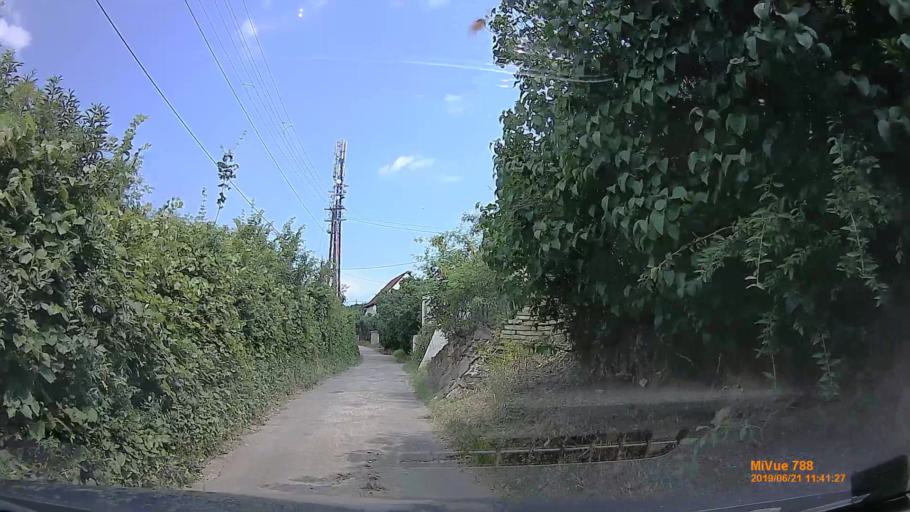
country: HU
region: Baranya
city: Pellerd
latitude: 46.0727
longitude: 18.1789
